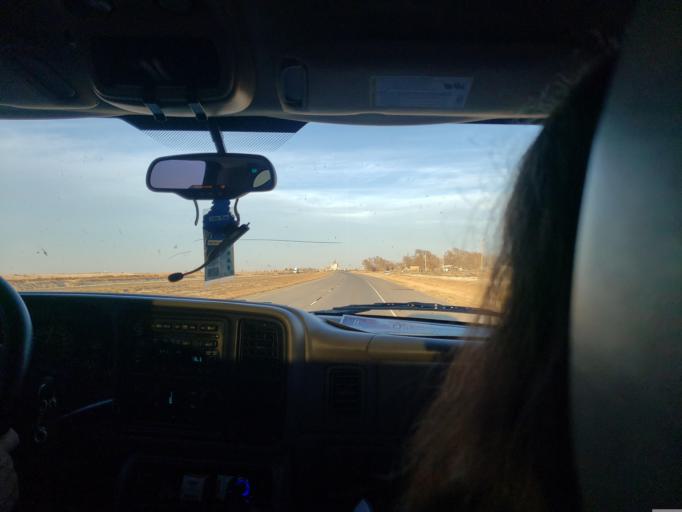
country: US
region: Oklahoma
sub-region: Texas County
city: Guymon
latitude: 36.7568
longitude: -101.3608
